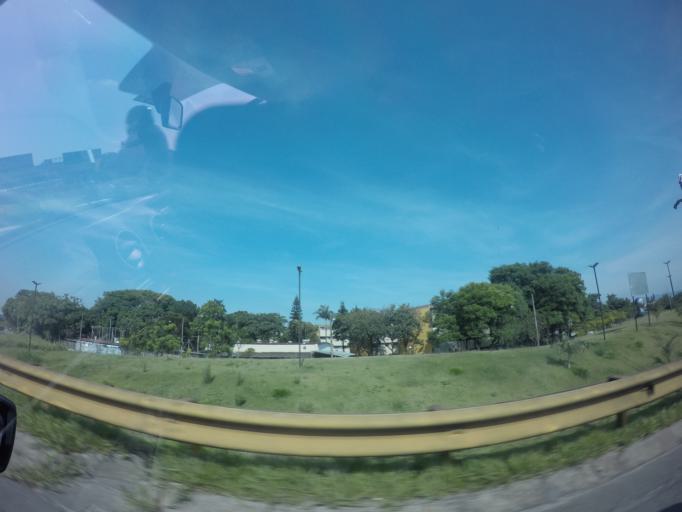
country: BR
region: Sao Paulo
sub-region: Guarulhos
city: Guarulhos
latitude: -23.4610
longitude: -46.4916
